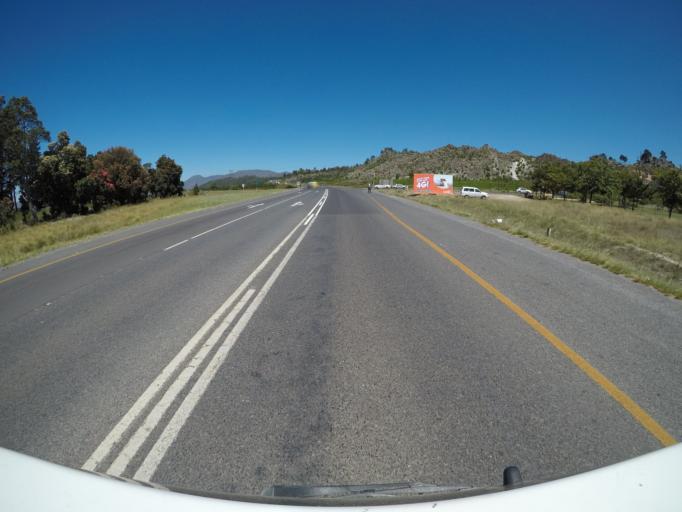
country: ZA
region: Western Cape
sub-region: Overberg District Municipality
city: Grabouw
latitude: -34.1628
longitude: 19.0093
